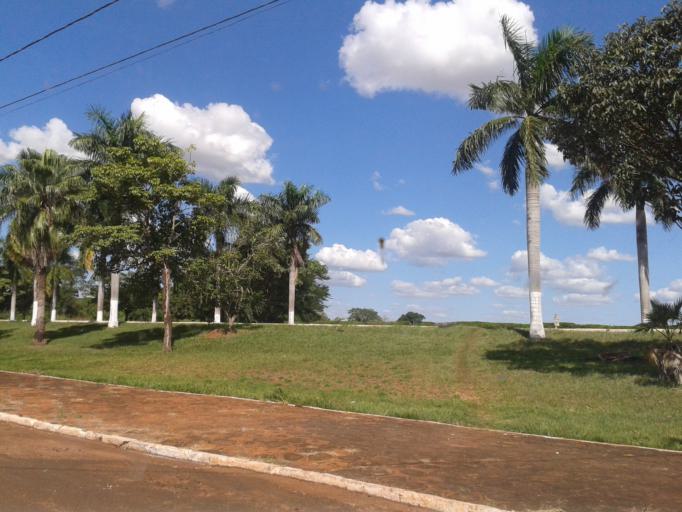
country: BR
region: Minas Gerais
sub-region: Santa Vitoria
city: Santa Vitoria
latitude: -18.6957
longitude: -49.9359
